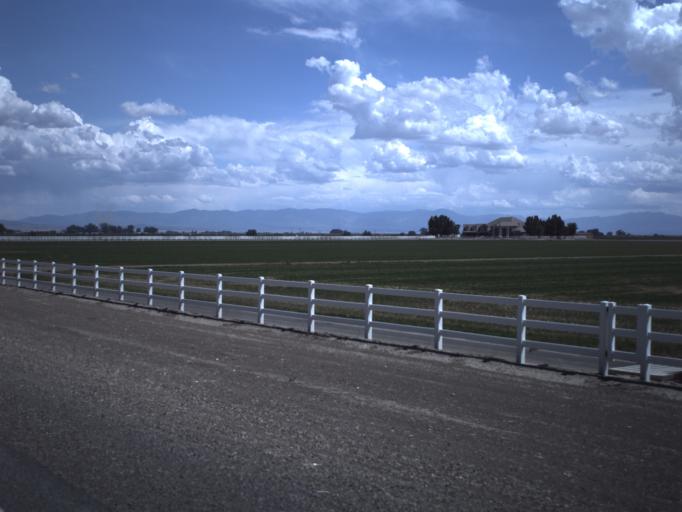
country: US
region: Utah
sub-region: Millard County
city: Delta
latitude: 39.3306
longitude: -112.6374
